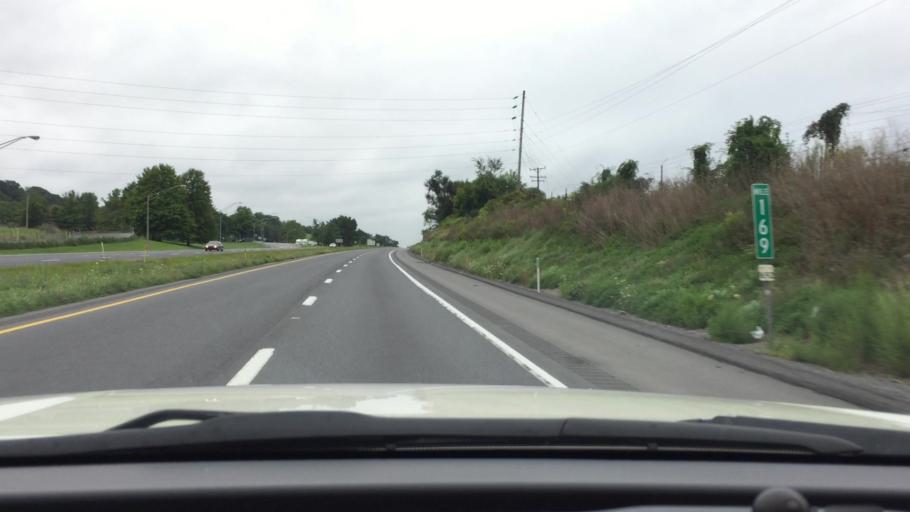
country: US
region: Maryland
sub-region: Washington County
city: Hancock
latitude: 39.7412
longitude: -78.1814
